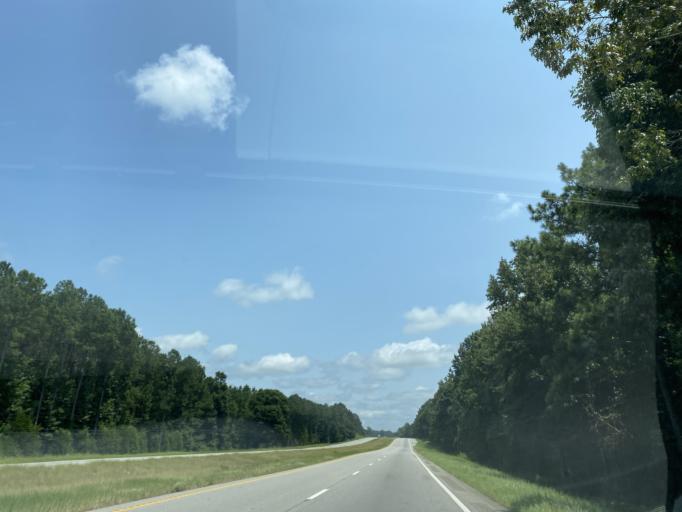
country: US
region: Georgia
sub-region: Telfair County
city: Lumber City
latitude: 31.9059
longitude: -82.6585
